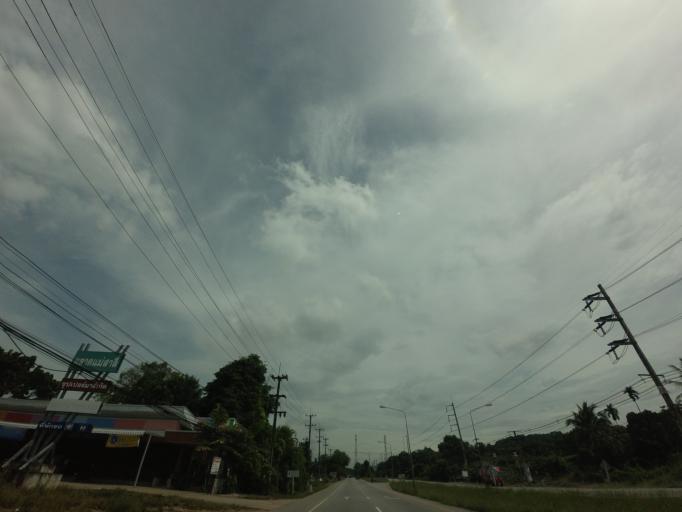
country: TH
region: Rayong
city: Klaeng
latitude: 12.7150
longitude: 101.5651
